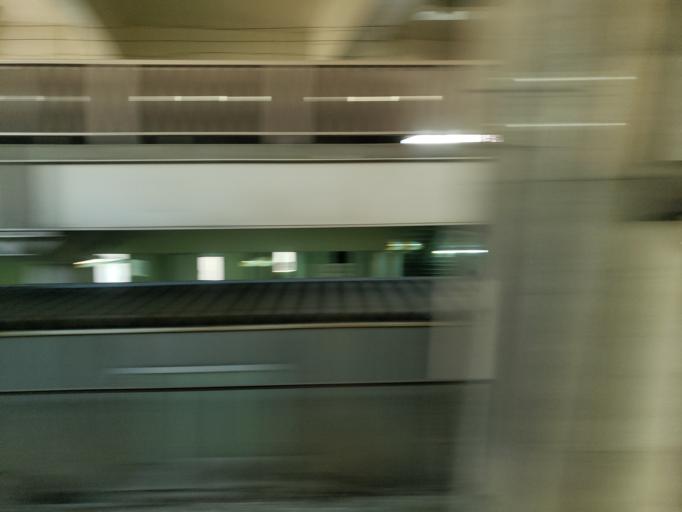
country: JP
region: Hyogo
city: Amagasaki
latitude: 34.7378
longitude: 135.3985
